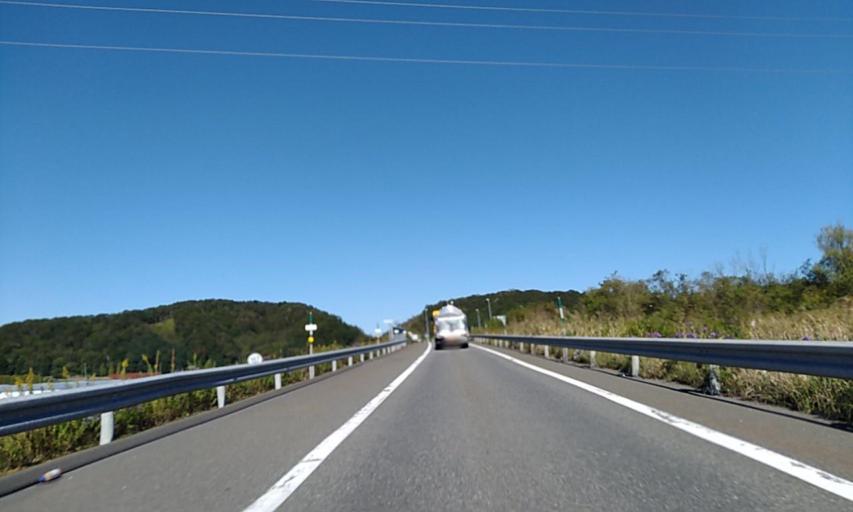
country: JP
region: Hokkaido
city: Shizunai-furukawacho
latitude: 42.5286
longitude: 142.0379
